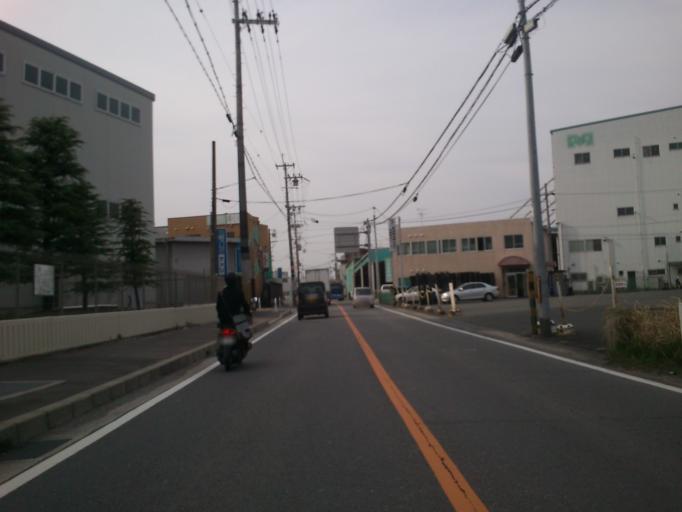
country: JP
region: Kyoto
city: Yawata
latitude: 34.8727
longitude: 135.7287
